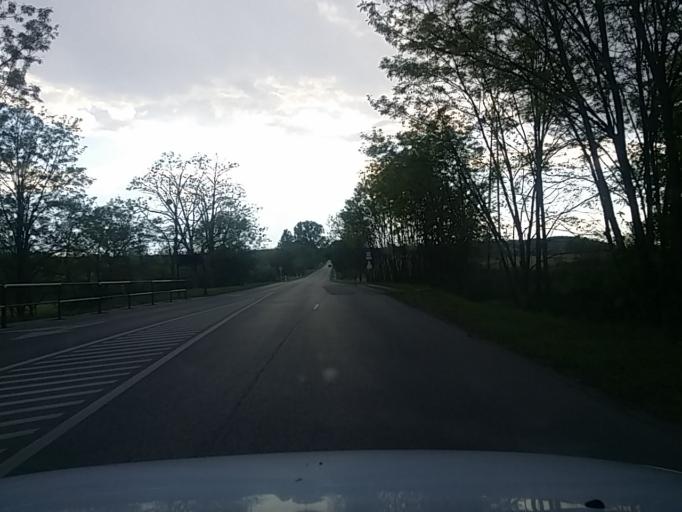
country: HU
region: Pest
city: Veresegyhaz
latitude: 47.6517
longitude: 19.2482
